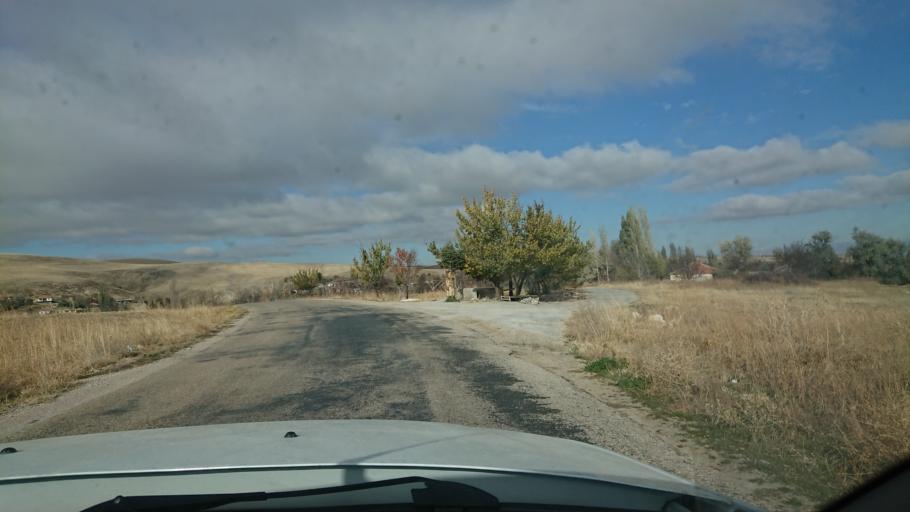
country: TR
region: Aksaray
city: Ortakoy
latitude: 38.8028
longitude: 33.9878
